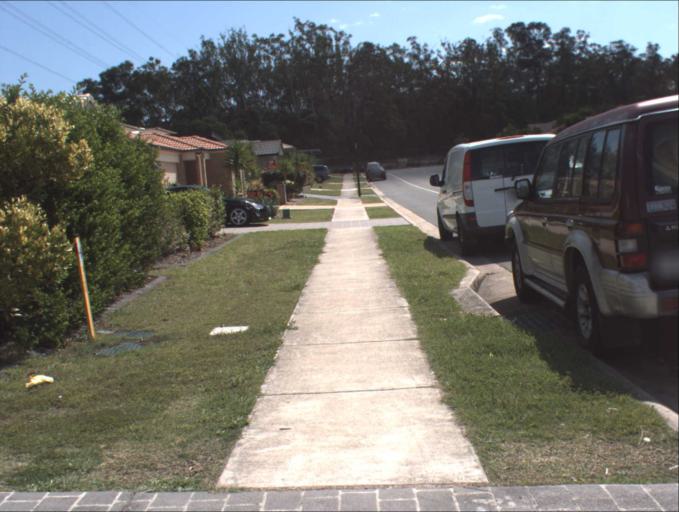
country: AU
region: Queensland
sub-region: Logan
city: Woodridge
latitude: -27.6587
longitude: 153.0743
